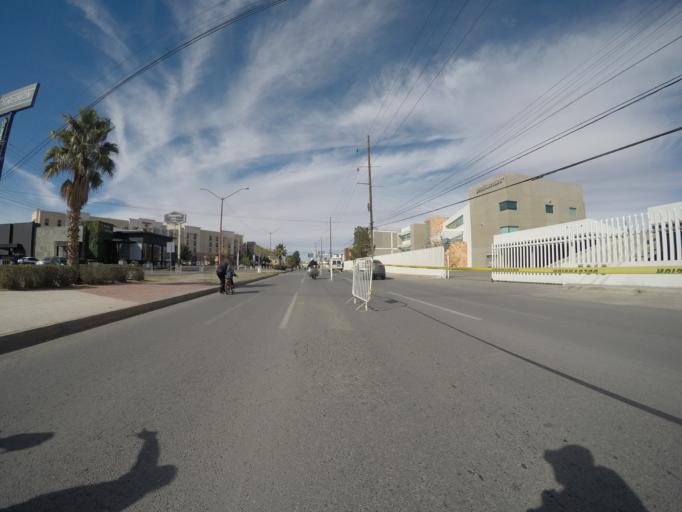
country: MX
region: Chihuahua
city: Ciudad Juarez
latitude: 31.7305
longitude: -106.4100
